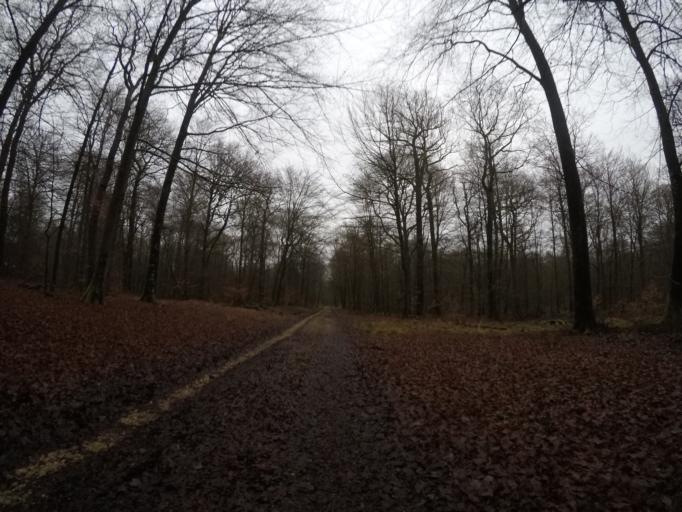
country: BE
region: Wallonia
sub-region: Province du Luxembourg
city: Fauvillers
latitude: 49.8136
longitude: 5.6389
